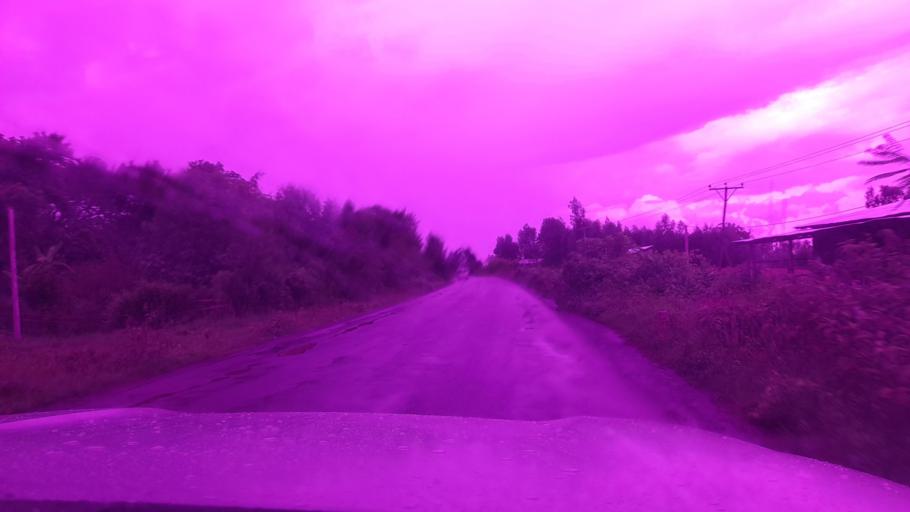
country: ET
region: Oromiya
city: Jima
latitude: 7.7074
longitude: 37.0738
